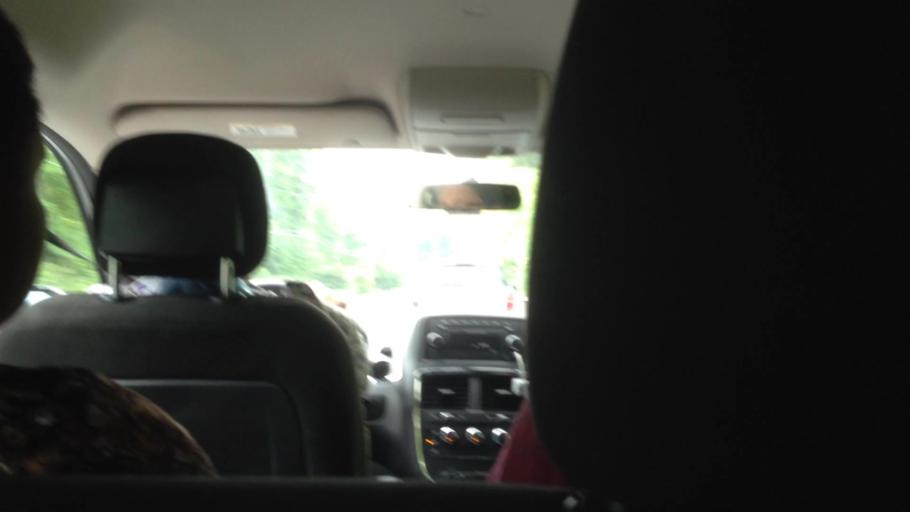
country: US
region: New York
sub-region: Dutchess County
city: Red Hook
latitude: 41.9934
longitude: -73.9107
